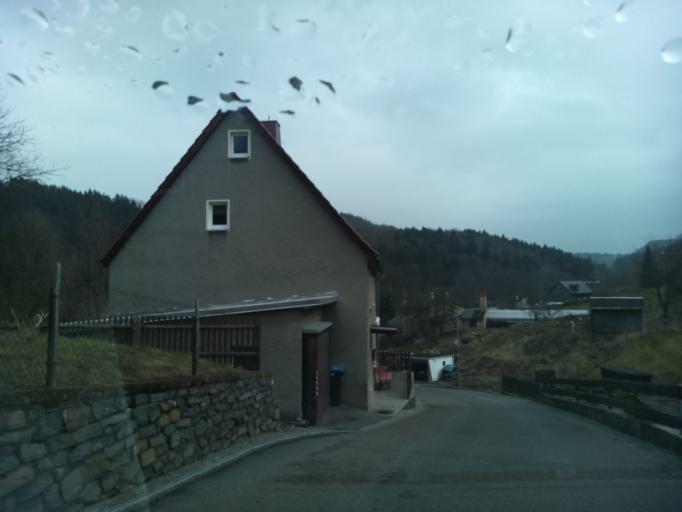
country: DE
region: Saxony
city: Grunhainichen
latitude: 50.7685
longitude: 13.1605
